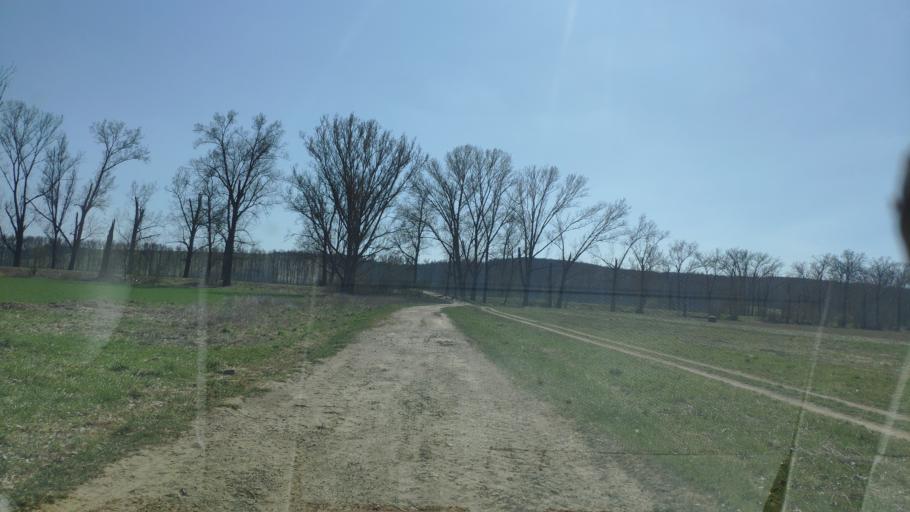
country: SK
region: Kosicky
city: Moldava nad Bodvou
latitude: 48.5737
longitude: 20.9470
